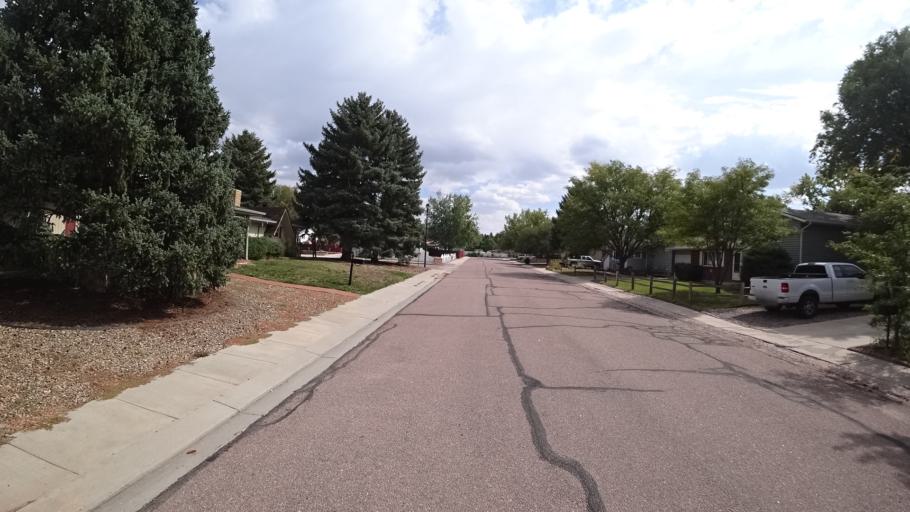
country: US
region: Colorado
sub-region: El Paso County
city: Cimarron Hills
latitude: 38.8493
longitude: -104.7402
